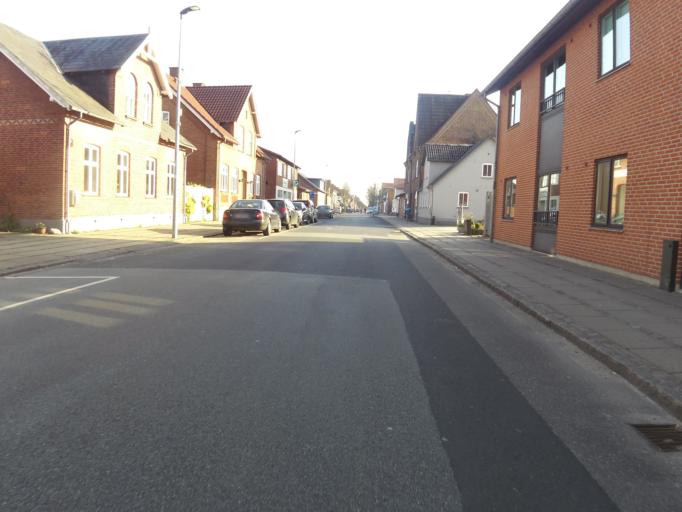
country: DK
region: South Denmark
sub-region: Vejen Kommune
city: Vejen
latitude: 55.4809
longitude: 9.1399
